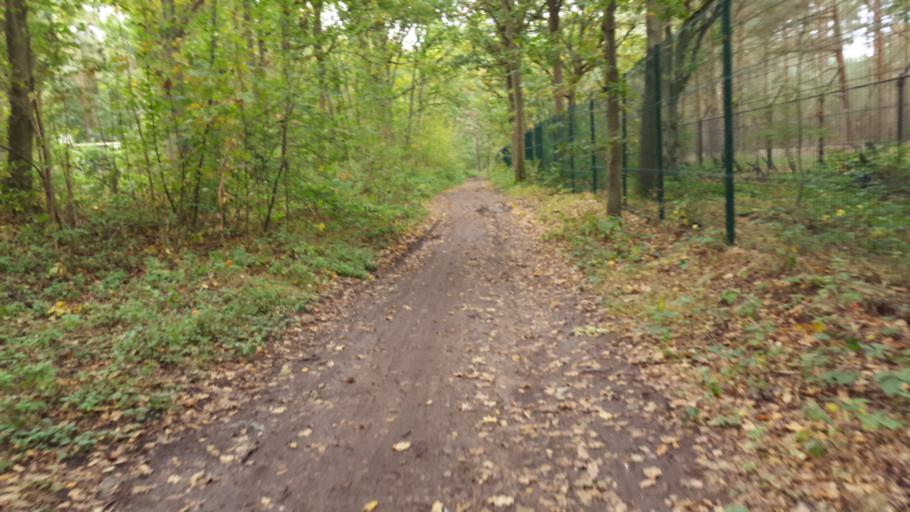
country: GB
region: England
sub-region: Norfolk
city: Weeting
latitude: 52.3957
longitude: 0.6335
